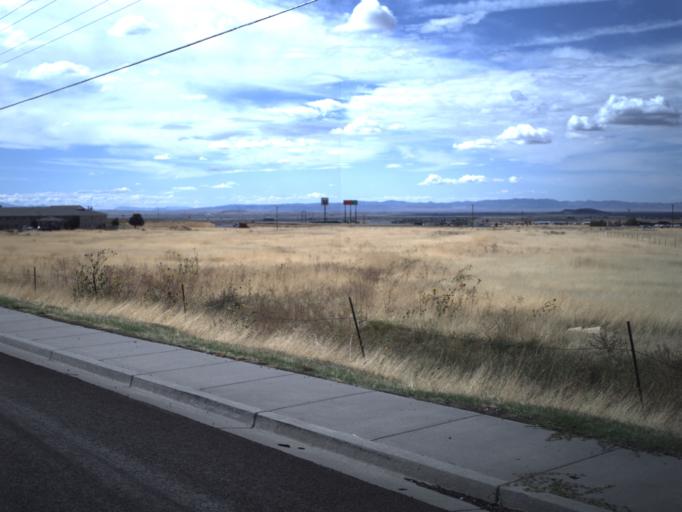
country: US
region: Utah
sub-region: Millard County
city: Fillmore
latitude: 38.9513
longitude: -112.3431
